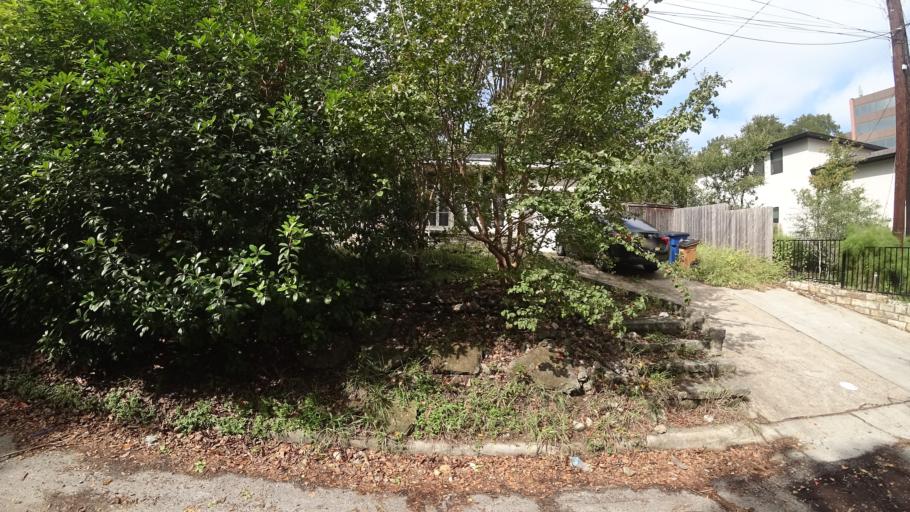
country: US
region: Texas
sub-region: Travis County
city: Austin
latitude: 30.2580
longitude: -97.7534
